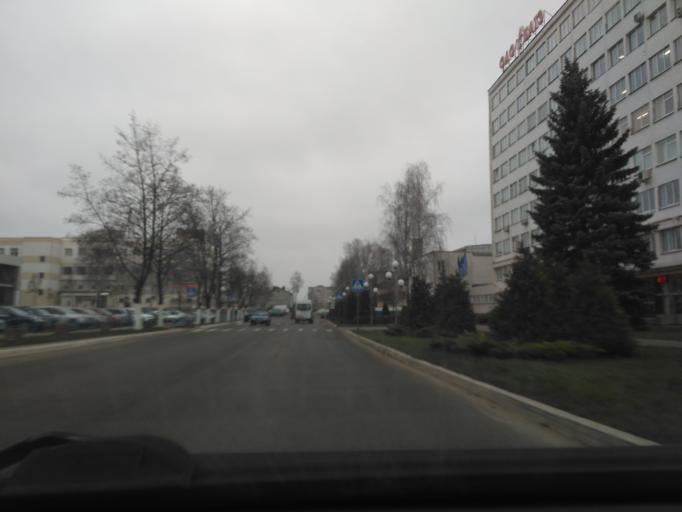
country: BY
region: Minsk
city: Horad Barysaw
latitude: 54.2121
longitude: 28.4911
